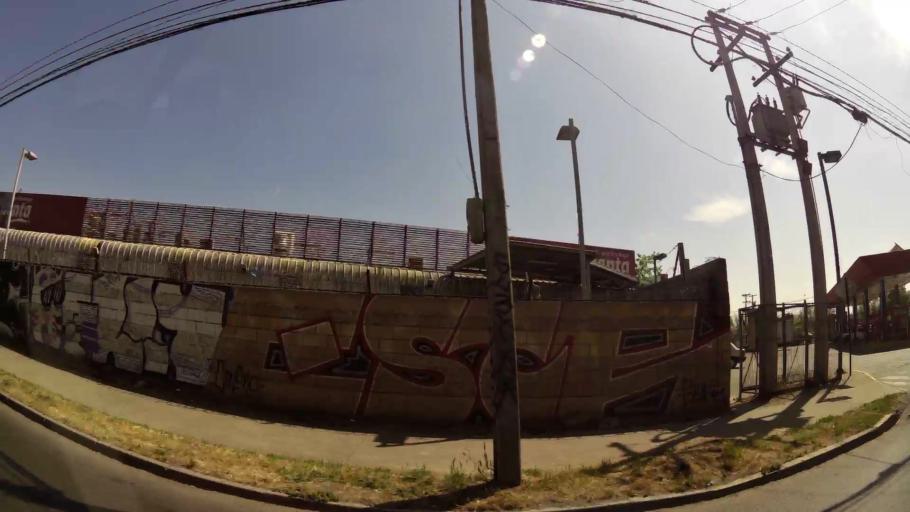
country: CL
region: Santiago Metropolitan
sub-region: Provincia de Santiago
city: Villa Presidente Frei, Nunoa, Santiago, Chile
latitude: -33.4702
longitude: -70.5529
